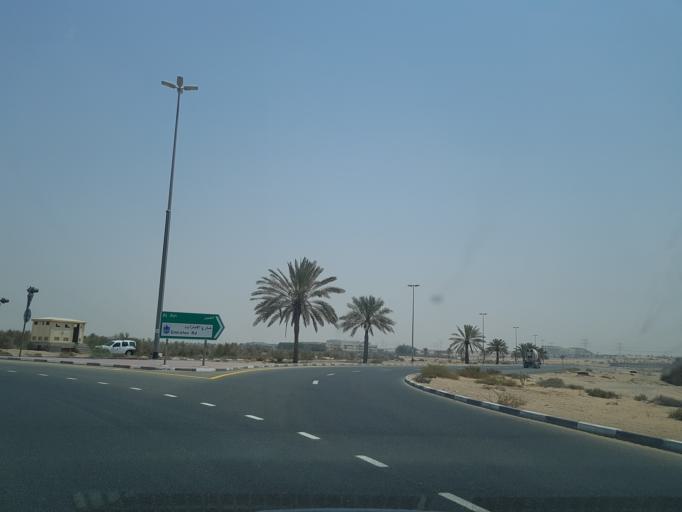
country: AE
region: Ash Shariqah
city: Sharjah
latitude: 25.1091
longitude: 55.3994
